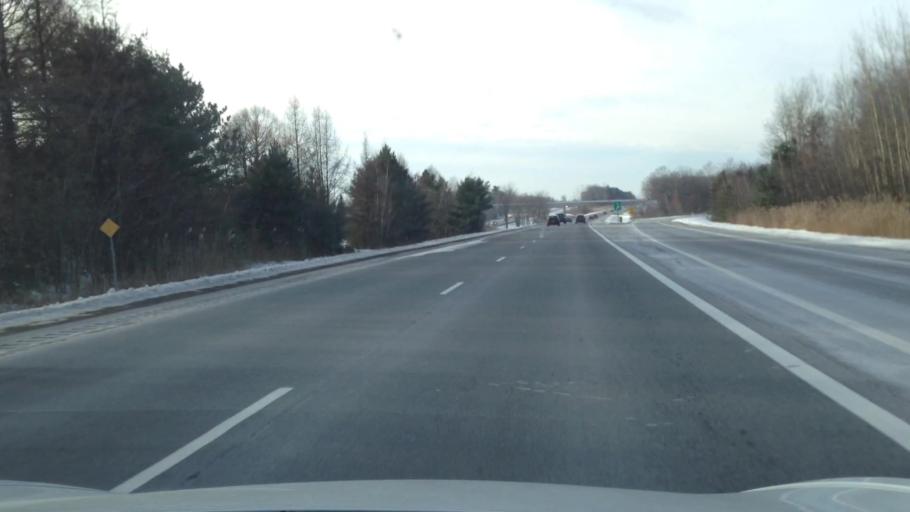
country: CA
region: Quebec
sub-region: Laurentides
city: Brownsburg-Chatham
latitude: 45.5522
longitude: -74.4441
